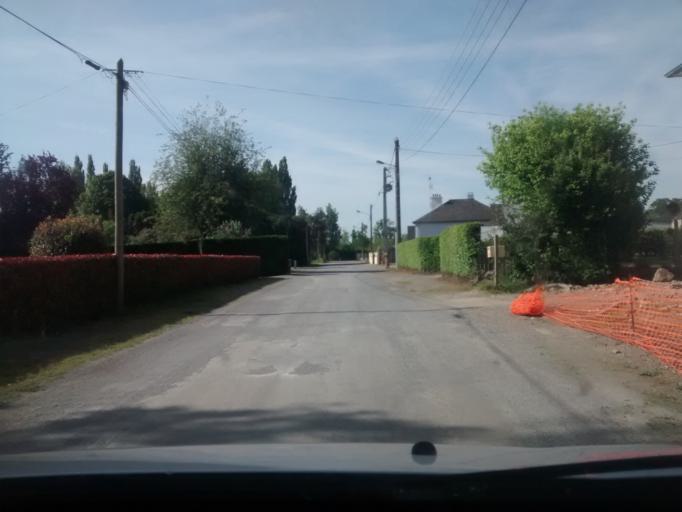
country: FR
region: Brittany
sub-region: Departement d'Ille-et-Vilaine
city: Fougeres
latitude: 48.3442
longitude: -1.2128
